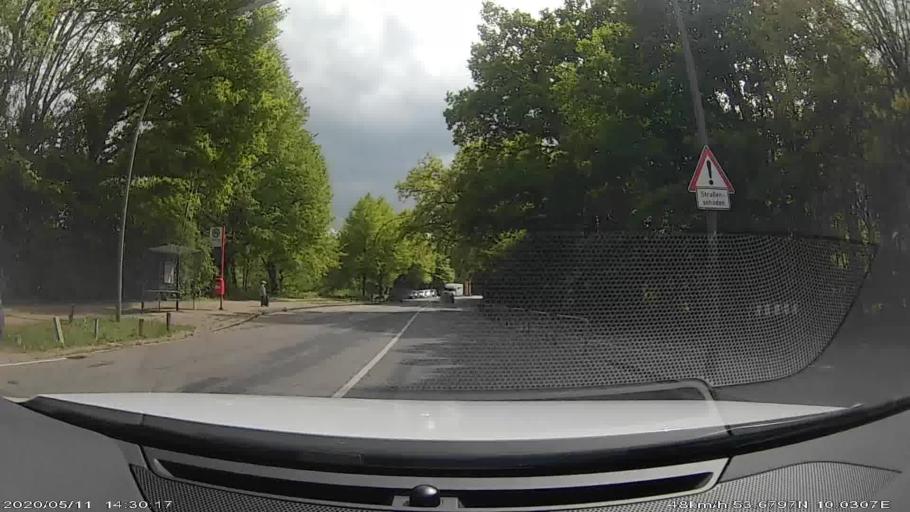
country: DE
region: Hamburg
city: Langenhorn
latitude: 53.6700
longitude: 10.0261
